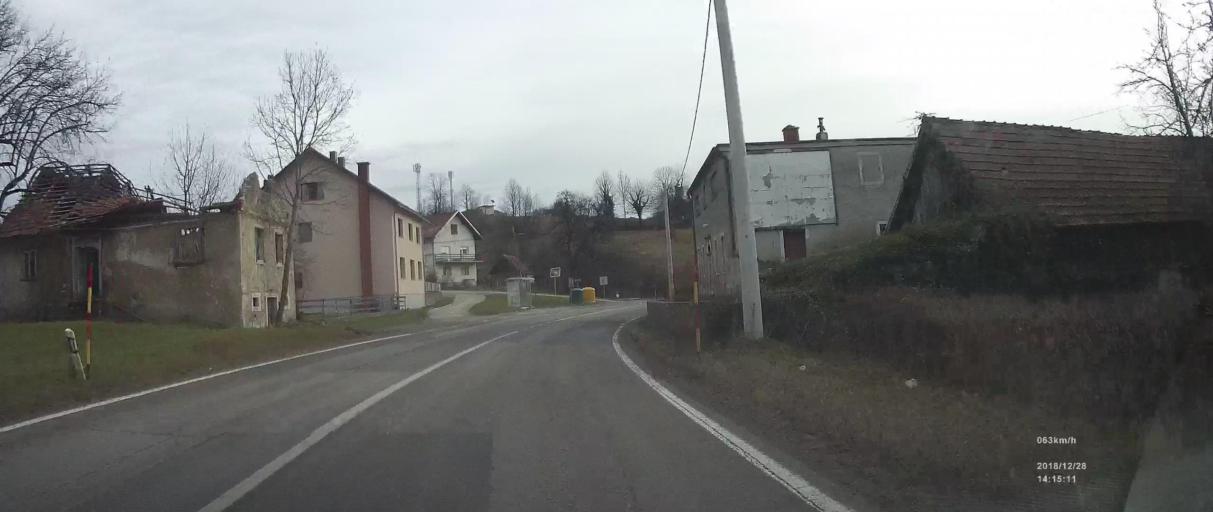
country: HR
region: Primorsko-Goranska
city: Vrbovsko
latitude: 45.4265
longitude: 15.0259
